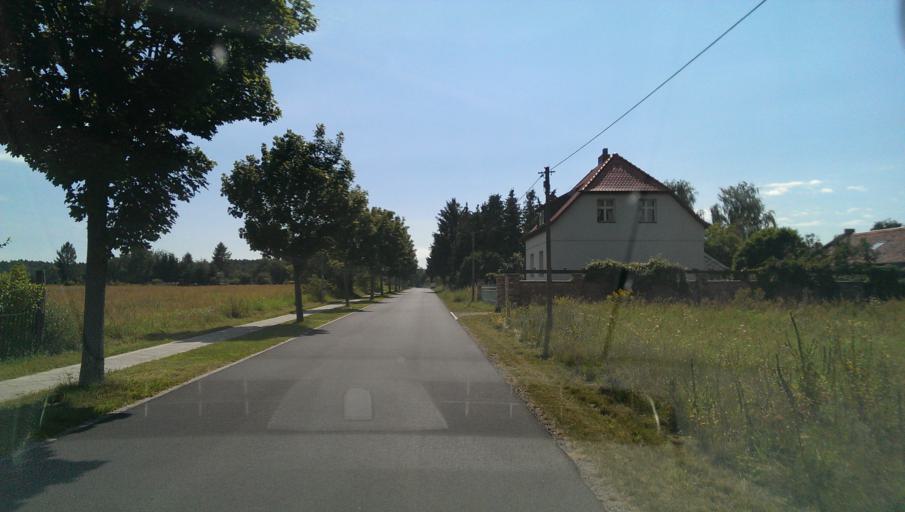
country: DE
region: Brandenburg
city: Michendorf
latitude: 52.3097
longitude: 13.0627
